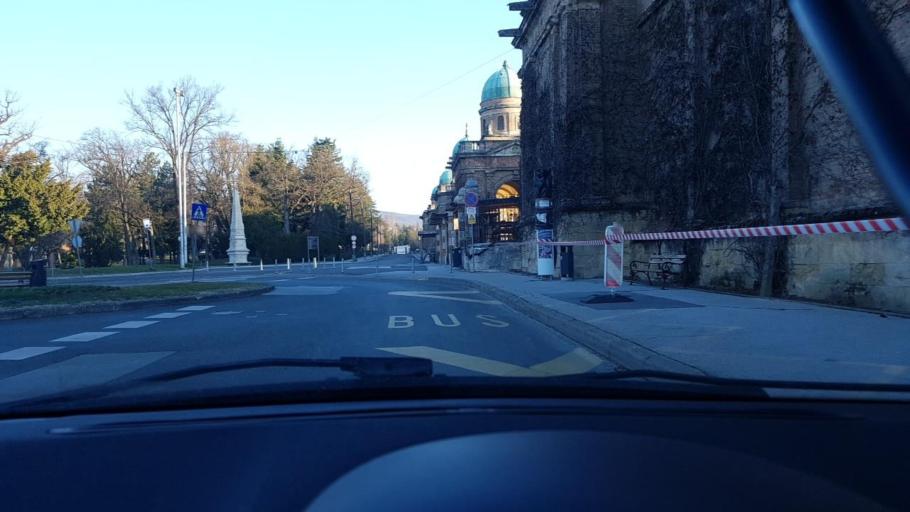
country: HR
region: Grad Zagreb
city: Zagreb
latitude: 45.8354
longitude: 15.9840
